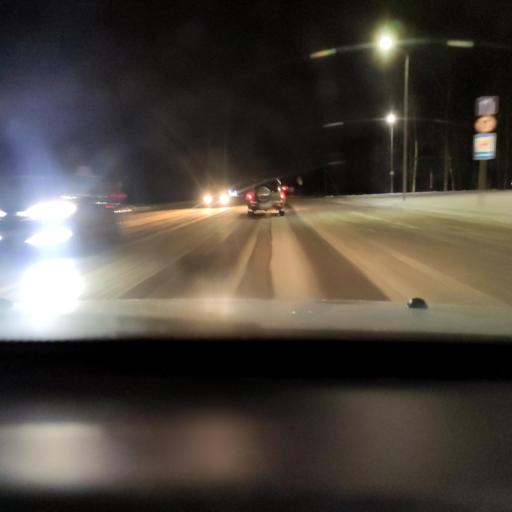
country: RU
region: Perm
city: Polazna
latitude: 58.1445
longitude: 56.4198
